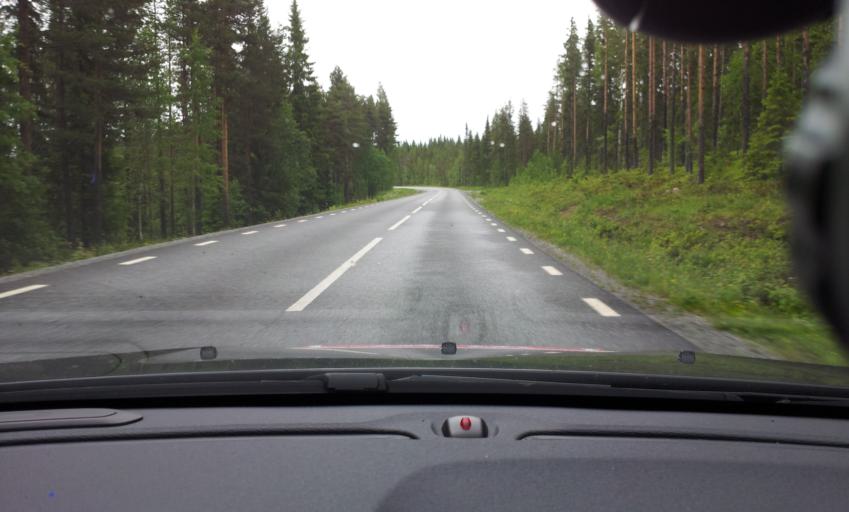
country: SE
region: Jaemtland
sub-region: OEstersunds Kommun
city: Lit
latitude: 63.7308
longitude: 14.7292
